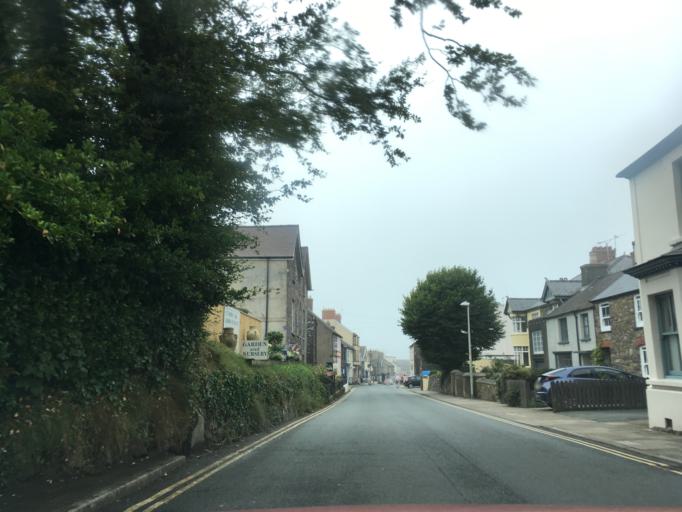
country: GB
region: Wales
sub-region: Pembrokeshire
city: Saint David's
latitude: 51.8807
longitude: -5.2620
